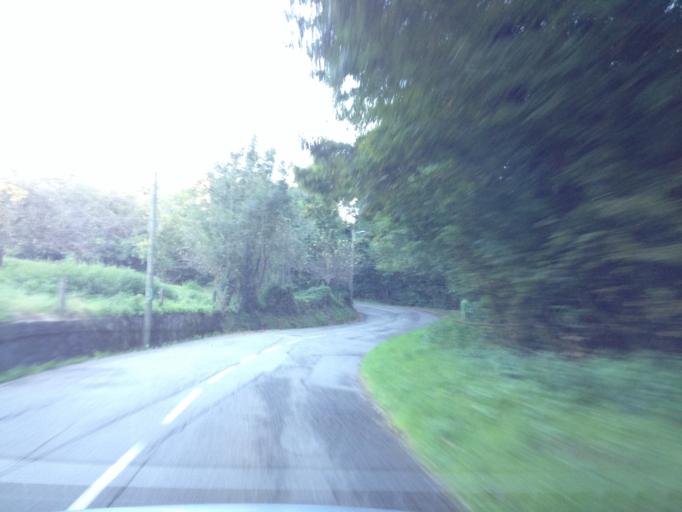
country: FR
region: Rhone-Alpes
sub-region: Departement de la Savoie
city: La Motte-Servolex
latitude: 45.6072
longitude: 5.8972
